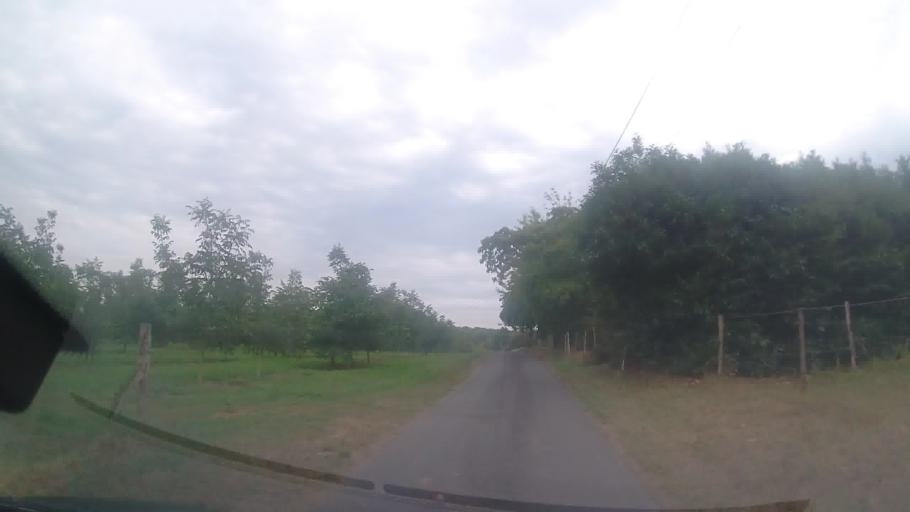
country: FR
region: Aquitaine
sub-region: Departement de la Dordogne
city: Eyvigues-et-Eybenes
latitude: 44.8374
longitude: 1.3580
